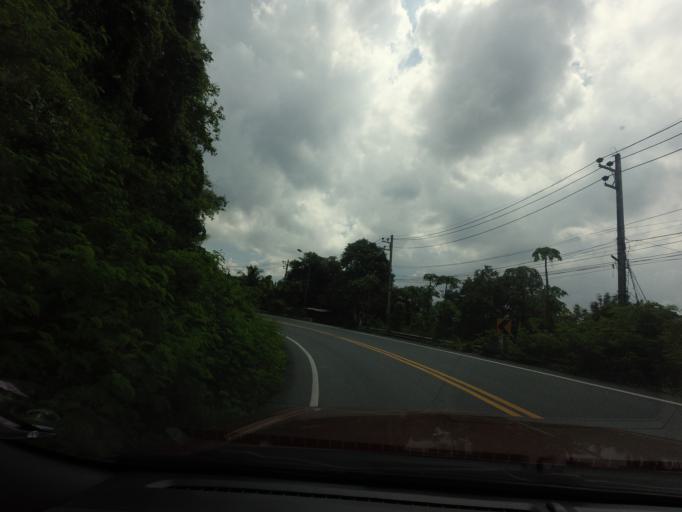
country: TH
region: Yala
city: Than To
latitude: 6.0404
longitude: 101.2087
